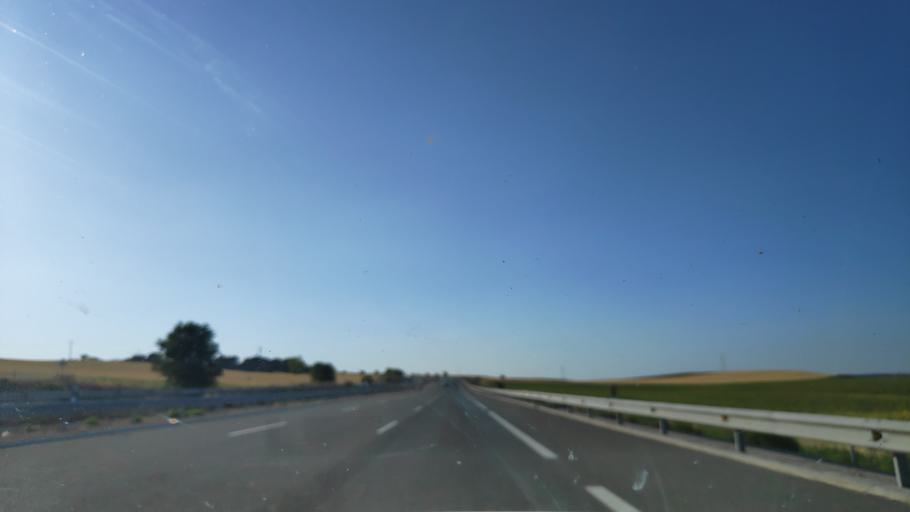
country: ES
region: Castille-La Mancha
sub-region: Provincia de Cuenca
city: Cervera del Llano
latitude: 39.8080
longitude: -2.4607
